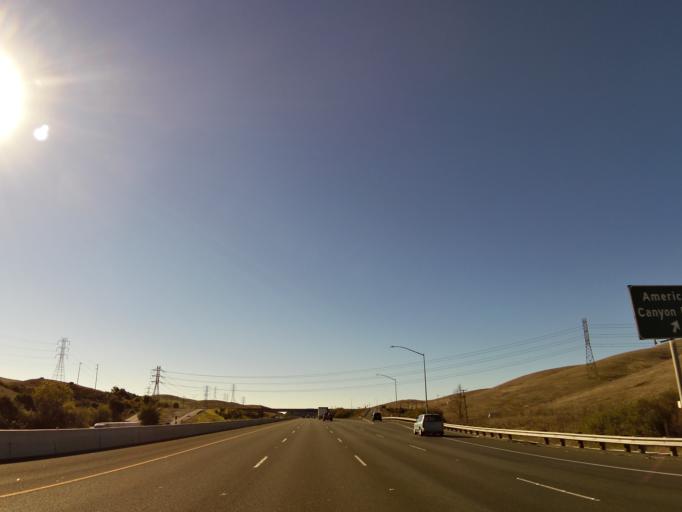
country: US
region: California
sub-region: Napa County
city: American Canyon
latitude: 38.1721
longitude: -122.1965
